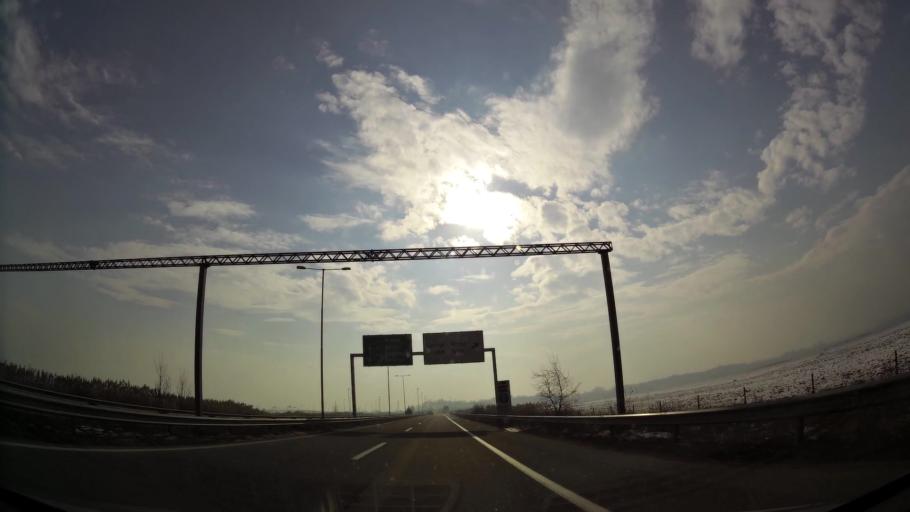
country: MK
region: Aracinovo
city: Arachinovo
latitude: 42.0011
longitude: 21.5336
